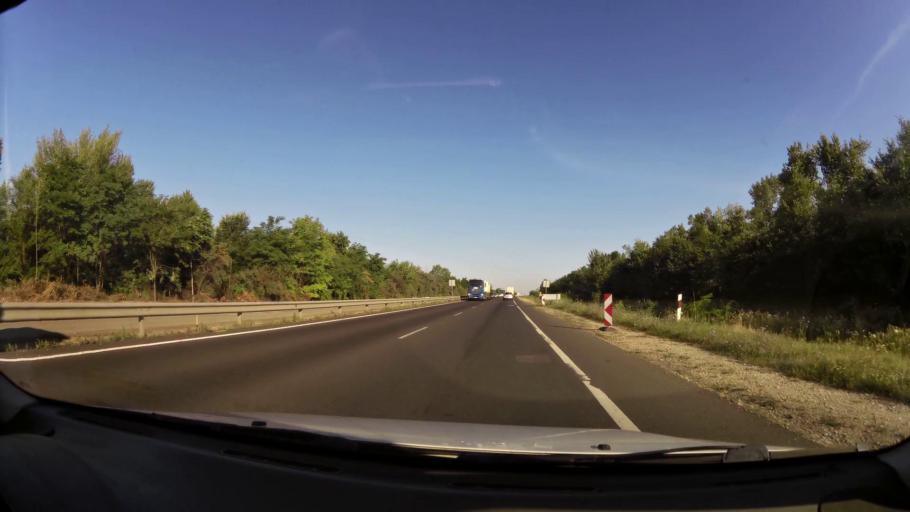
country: HU
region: Pest
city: Cegledbercel
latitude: 47.2229
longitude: 19.6918
